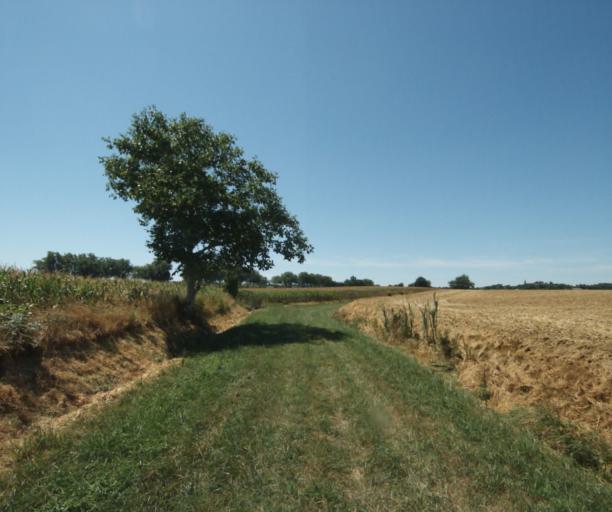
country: FR
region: Midi-Pyrenees
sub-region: Departement de la Haute-Garonne
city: Saint-Felix-Lauragais
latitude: 43.4755
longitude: 1.9408
